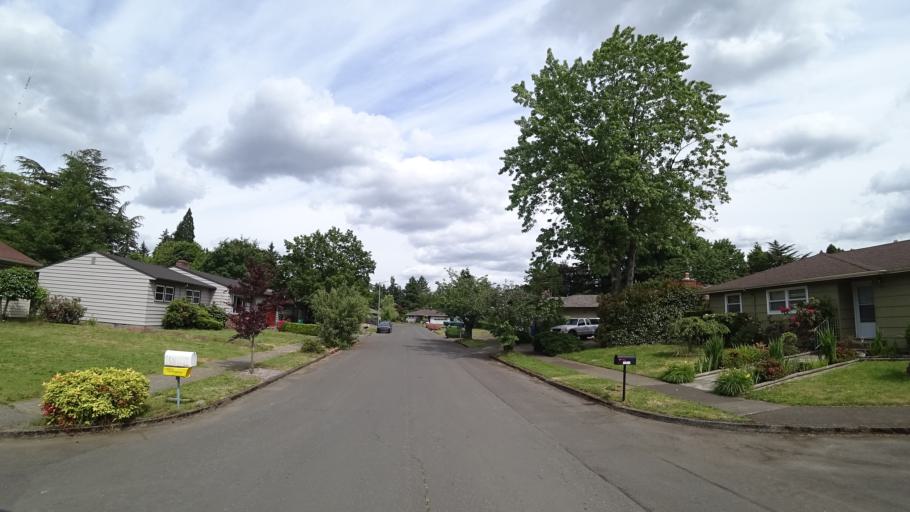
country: US
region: Oregon
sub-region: Multnomah County
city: Lents
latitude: 45.4882
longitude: -122.5528
